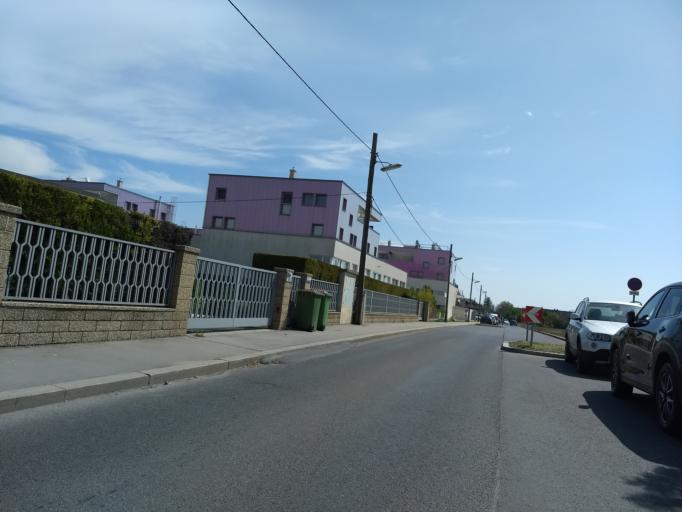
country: AT
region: Lower Austria
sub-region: Politischer Bezirk Ganserndorf
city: Aderklaa
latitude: 48.2398
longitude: 16.4956
